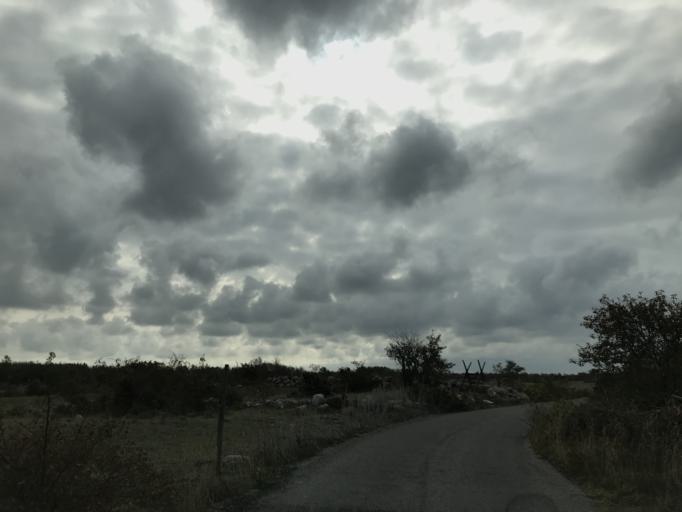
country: SE
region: Kalmar
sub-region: Borgholms Kommun
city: Borgholm
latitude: 57.0500
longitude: 16.8356
